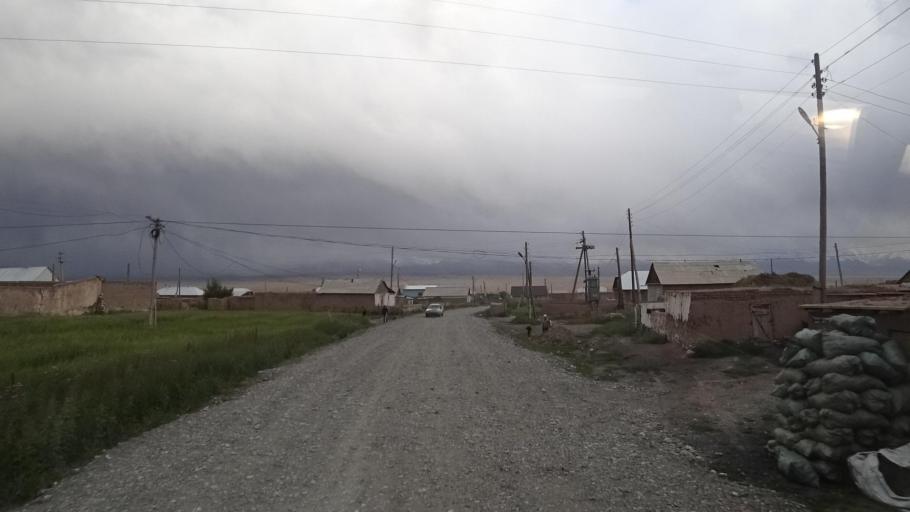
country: KG
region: Osh
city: Osh
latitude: 39.6773
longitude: 72.8822
